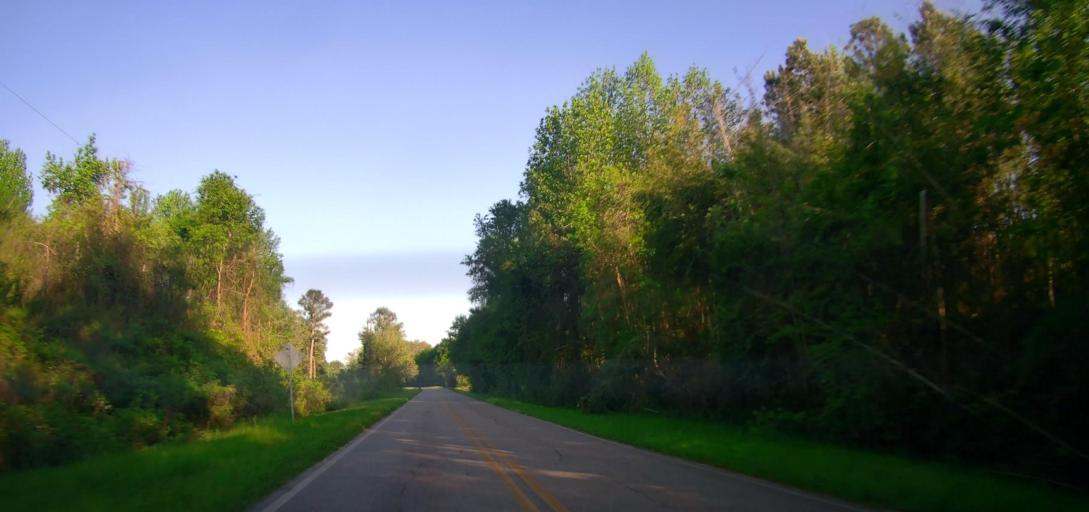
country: US
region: Georgia
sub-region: Macon County
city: Oglethorpe
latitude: 32.3034
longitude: -84.1038
